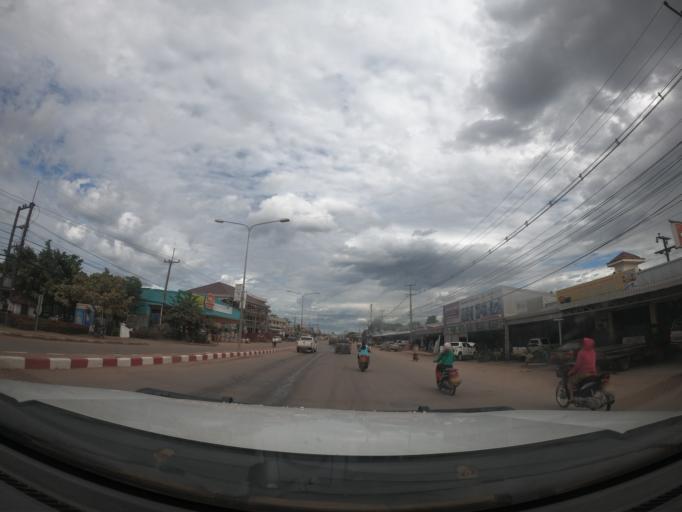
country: LA
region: Bolikhamxai
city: Muang Pakxan
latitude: 18.3936
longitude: 103.6510
